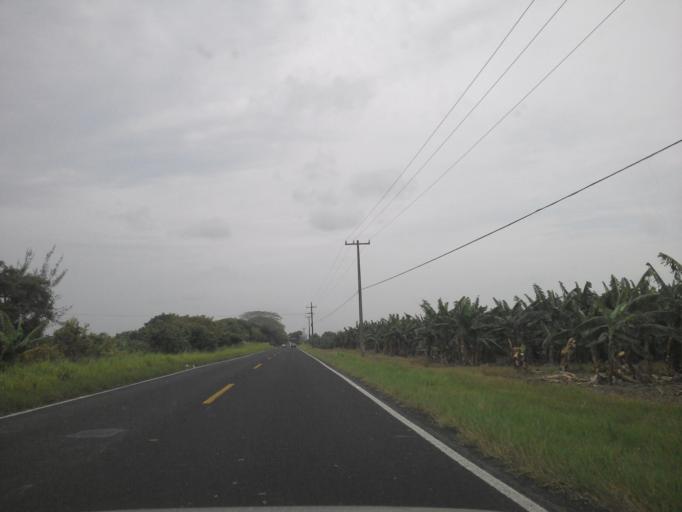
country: MX
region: Veracruz
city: Nautla
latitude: 20.2228
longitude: -96.7867
